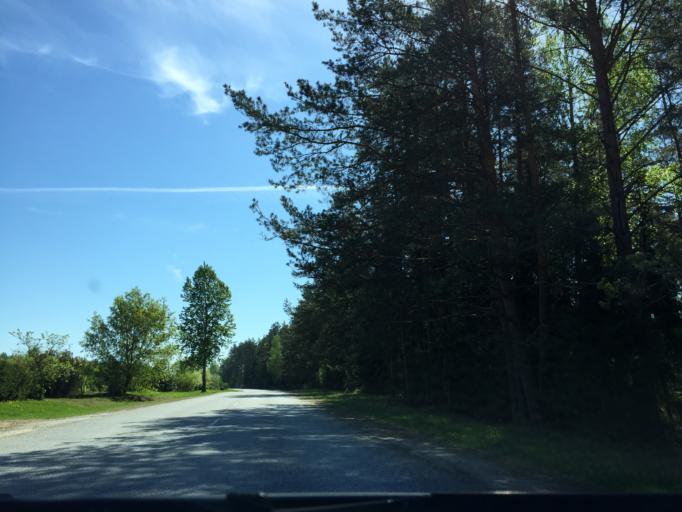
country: LV
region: Incukalns
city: Vangazi
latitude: 57.0114
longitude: 24.5341
